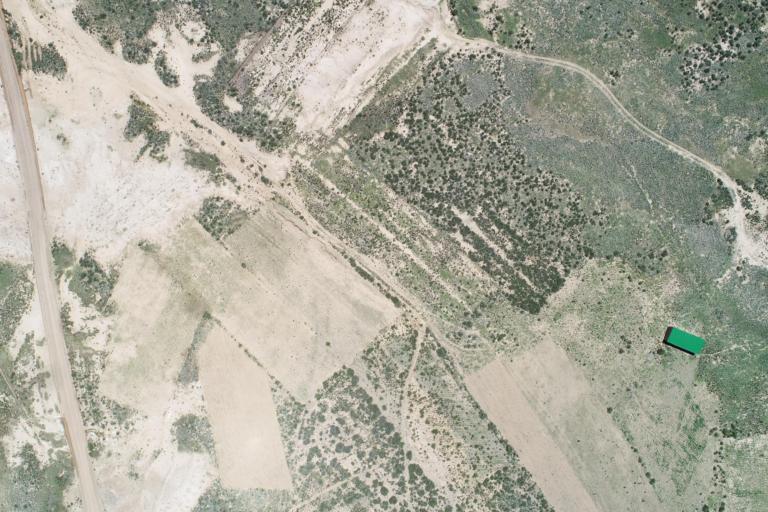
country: BO
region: La Paz
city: Curahuara de Carangas
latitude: -17.3178
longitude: -68.4993
